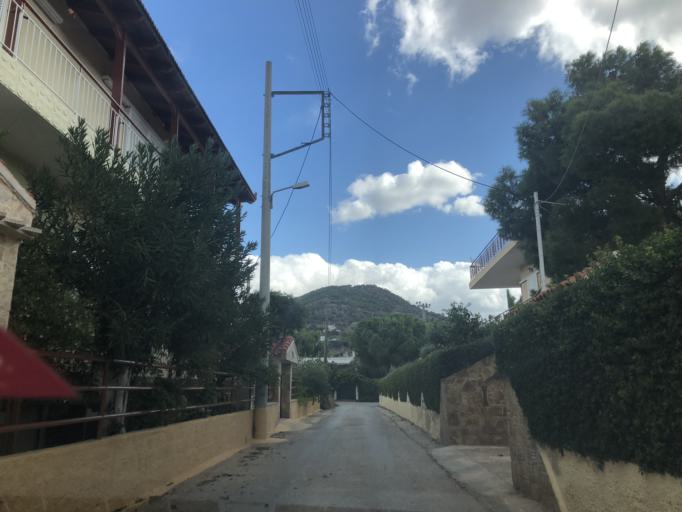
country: GR
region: Attica
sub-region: Nomarchia Anatolikis Attikis
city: Agia Marina
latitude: 37.8216
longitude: 23.8430
